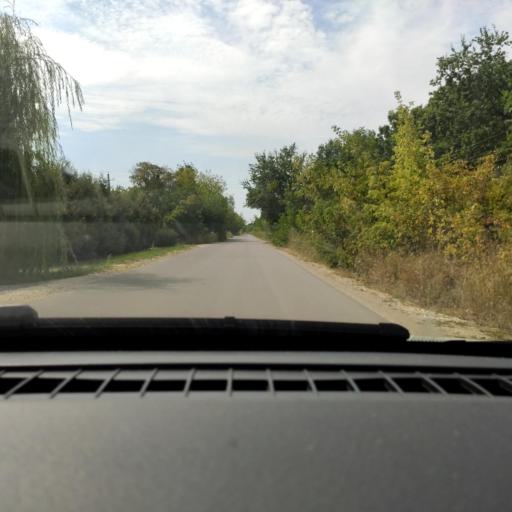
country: RU
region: Voronezj
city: Pridonskoy
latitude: 51.7390
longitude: 39.0679
